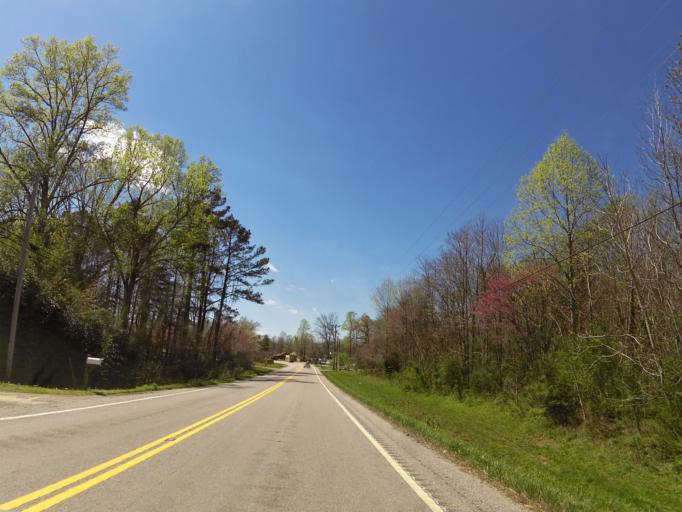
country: US
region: Tennessee
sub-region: DeKalb County
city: Smithville
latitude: 35.9764
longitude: -85.6994
